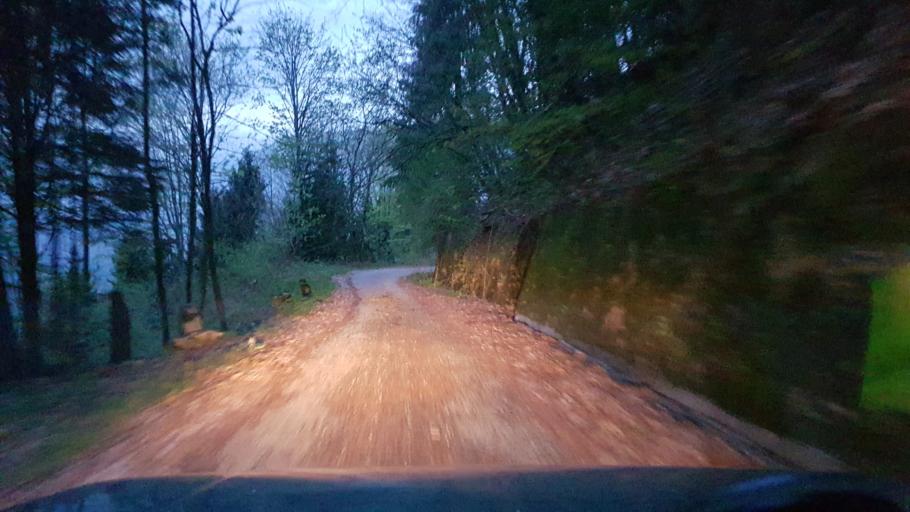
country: IT
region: Friuli Venezia Giulia
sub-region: Provincia di Udine
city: Taipana
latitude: 46.2329
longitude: 13.3541
